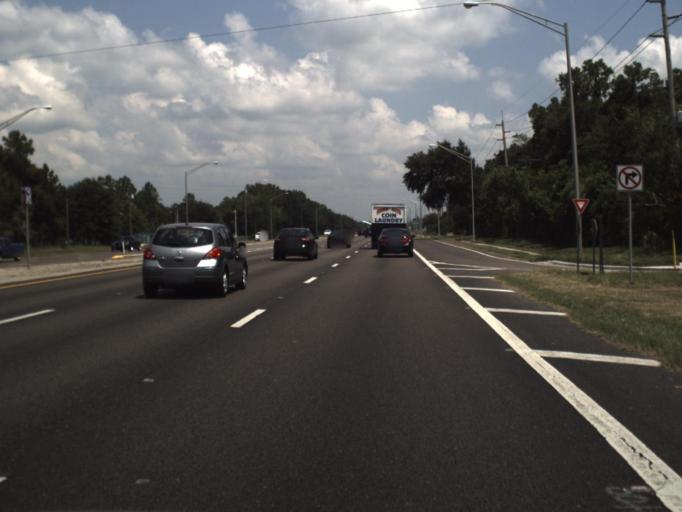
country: US
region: Florida
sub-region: Hillsborough County
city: Greater Northdale
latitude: 28.1186
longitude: -82.5024
